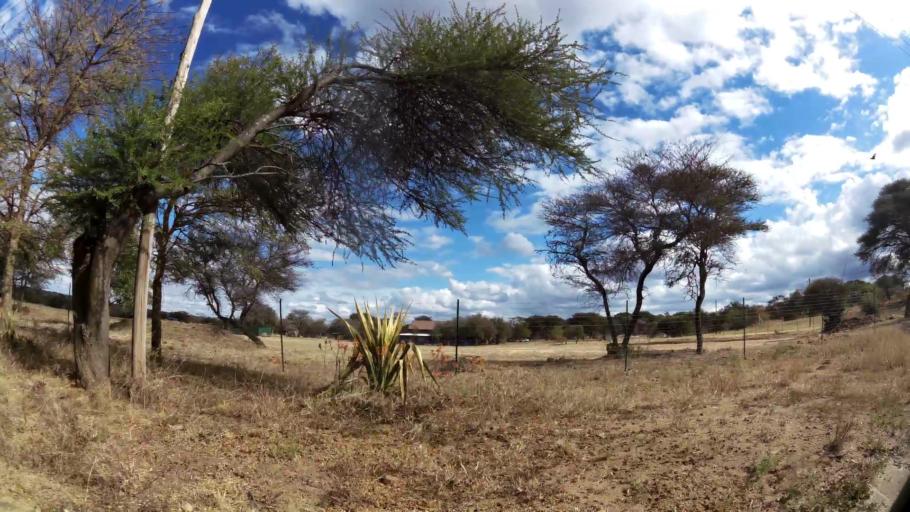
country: ZA
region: Limpopo
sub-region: Waterberg District Municipality
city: Modimolle
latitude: -24.7105
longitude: 28.4018
